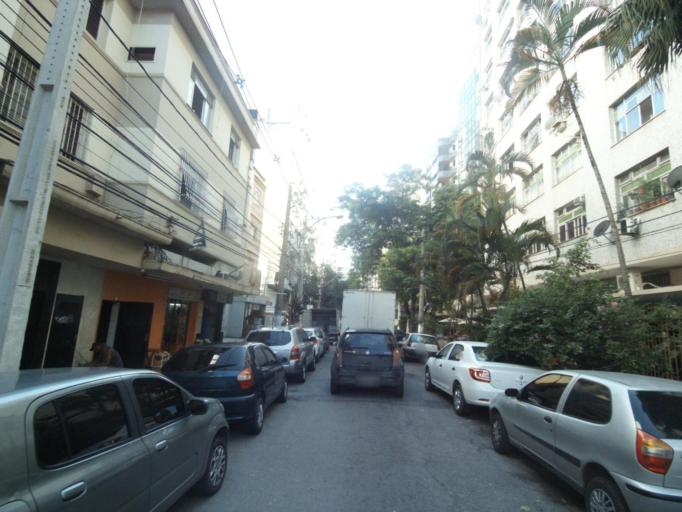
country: BR
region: Rio de Janeiro
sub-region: Niteroi
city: Niteroi
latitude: -22.9035
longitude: -43.1242
